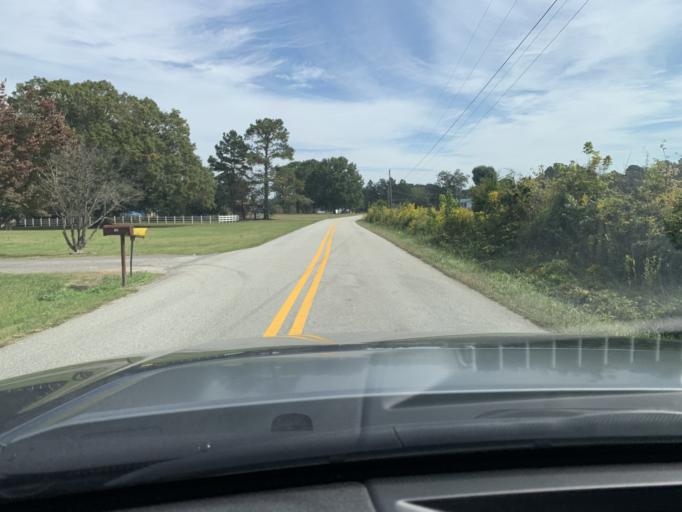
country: US
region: Georgia
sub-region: Polk County
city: Cedartown
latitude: 33.9711
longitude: -85.2667
